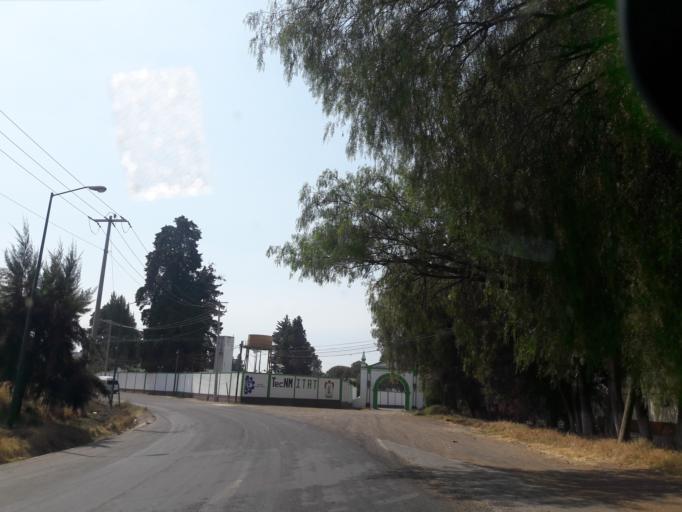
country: MX
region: Tlaxcala
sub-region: Ixtacuixtla de Mariano Matamoros
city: Villa Mariano Matamoros
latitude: 19.3108
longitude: -98.3856
